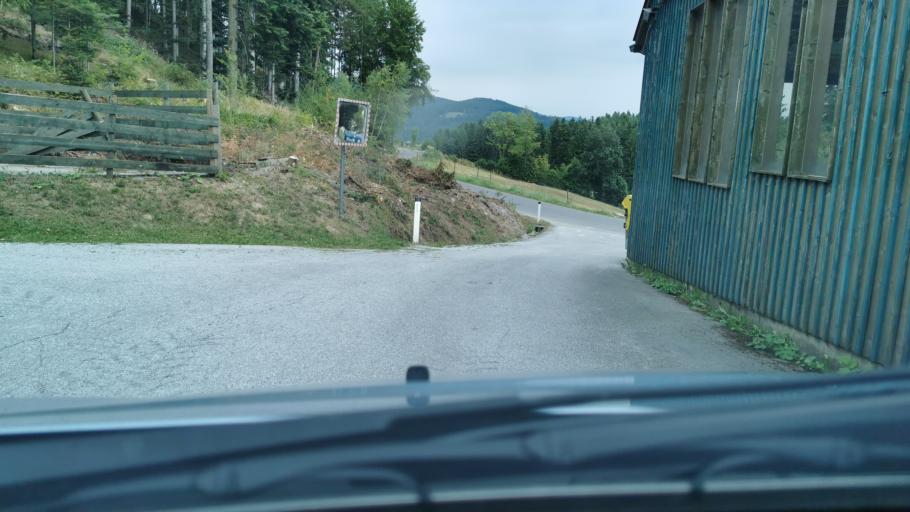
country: AT
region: Styria
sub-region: Politischer Bezirk Weiz
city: Birkfeld
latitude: 47.3926
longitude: 15.6719
